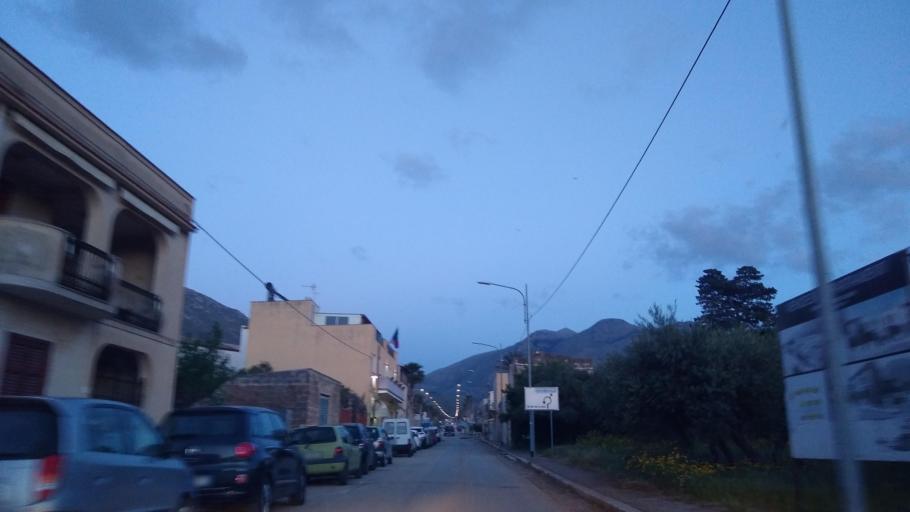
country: IT
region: Sicily
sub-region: Trapani
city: Castelluzzo
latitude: 38.1021
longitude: 12.7345
